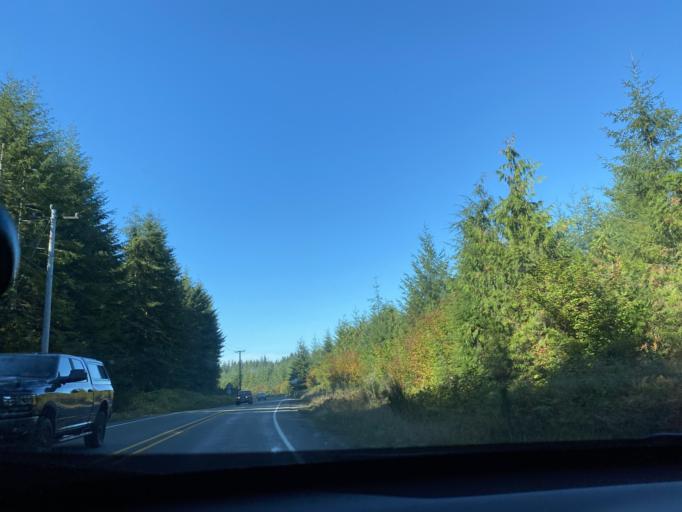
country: US
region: Washington
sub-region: Clallam County
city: Forks
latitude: 47.9540
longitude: -124.4531
